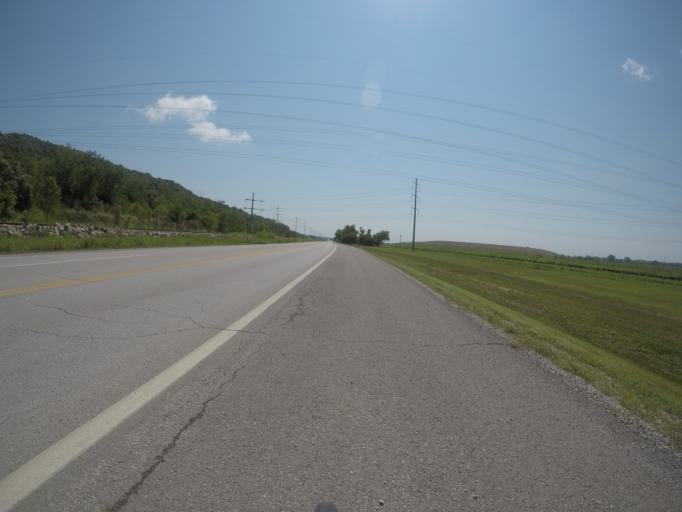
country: US
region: Missouri
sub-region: Platte County
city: Weston
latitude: 39.4581
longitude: -94.9674
